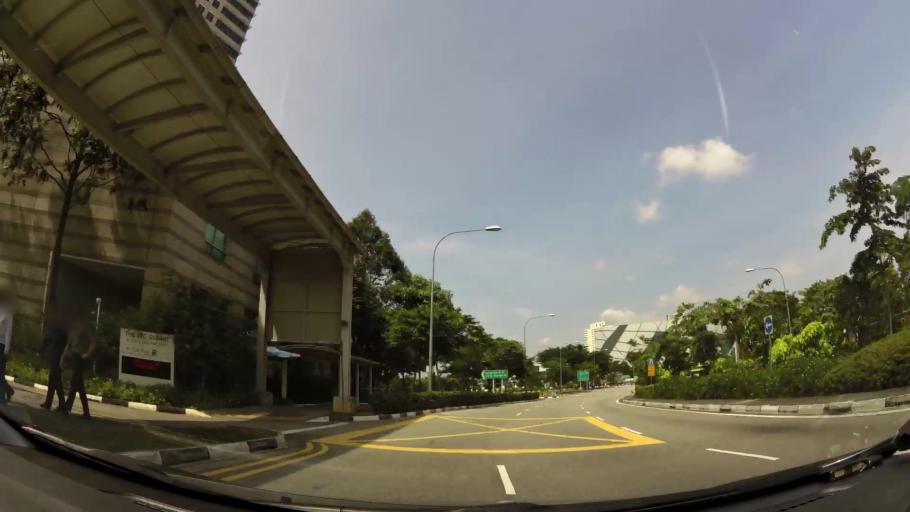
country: SG
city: Singapore
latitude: 1.3317
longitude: 103.7421
